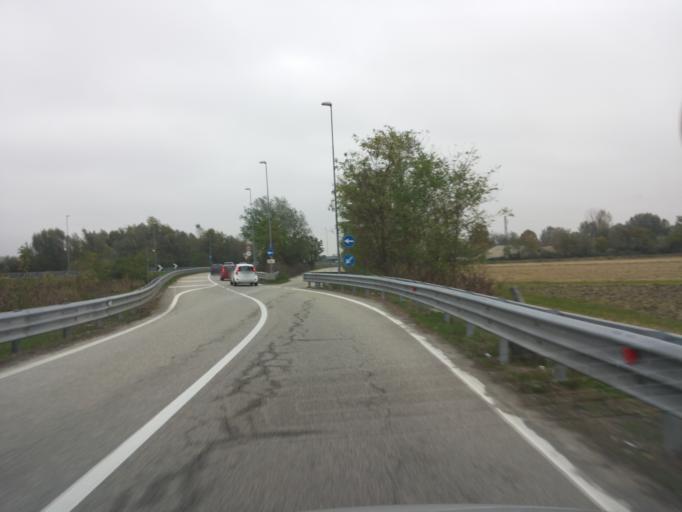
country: IT
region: Piedmont
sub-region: Provincia di Vercelli
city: Borgo Vercelli
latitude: 45.3640
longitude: 8.4793
